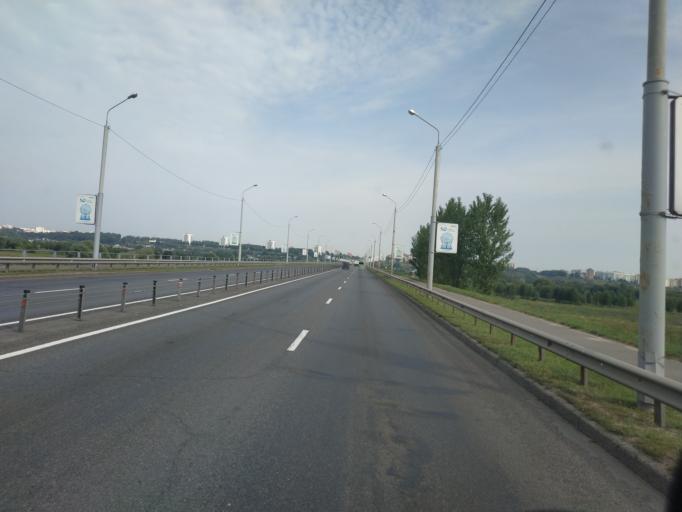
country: BY
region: Mogilev
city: Mahilyow
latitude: 53.8863
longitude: 30.3786
